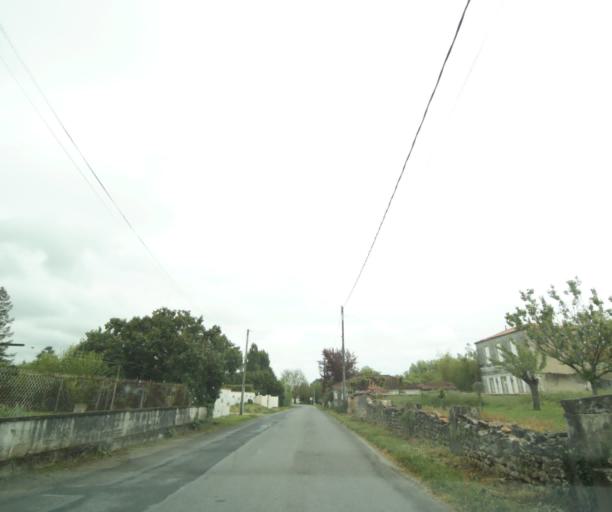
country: FR
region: Poitou-Charentes
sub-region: Departement de la Charente-Maritime
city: Chaniers
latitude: 45.6961
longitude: -0.5126
